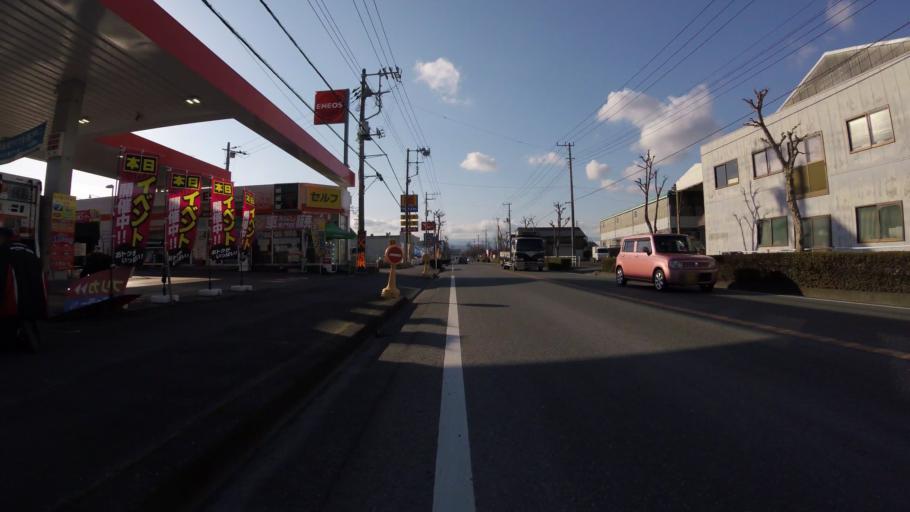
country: JP
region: Shizuoka
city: Fuji
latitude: 35.1591
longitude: 138.7181
